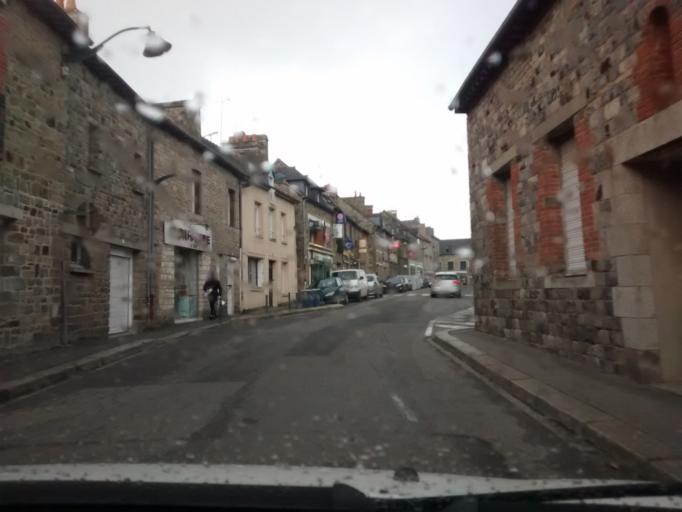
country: FR
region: Brittany
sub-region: Departement d'Ille-et-Vilaine
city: Liffre
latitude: 48.2131
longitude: -1.5056
